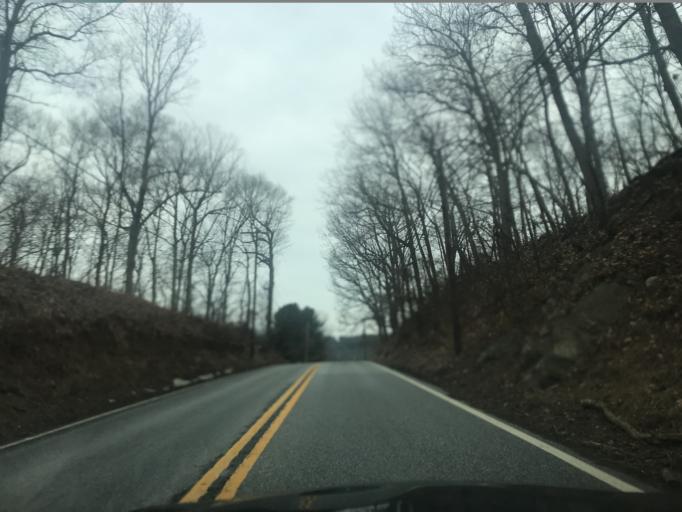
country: US
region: Maryland
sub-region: Harford County
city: Jarrettsville
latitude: 39.6973
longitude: -76.4613
